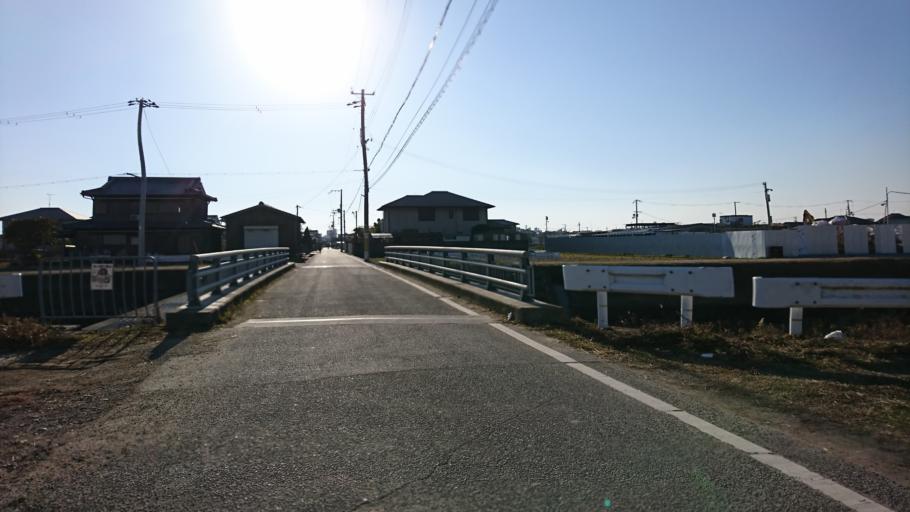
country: JP
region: Hyogo
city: Kakogawacho-honmachi
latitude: 34.7703
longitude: 134.8560
